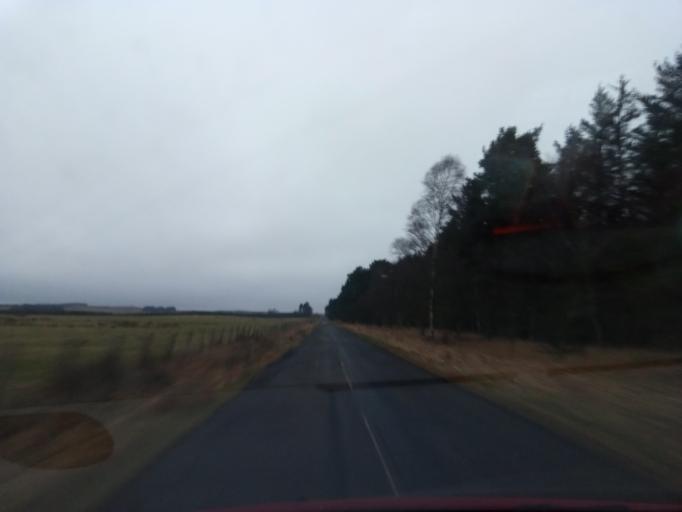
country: GB
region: England
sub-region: Northumberland
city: Rothley
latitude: 55.2024
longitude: -1.9978
